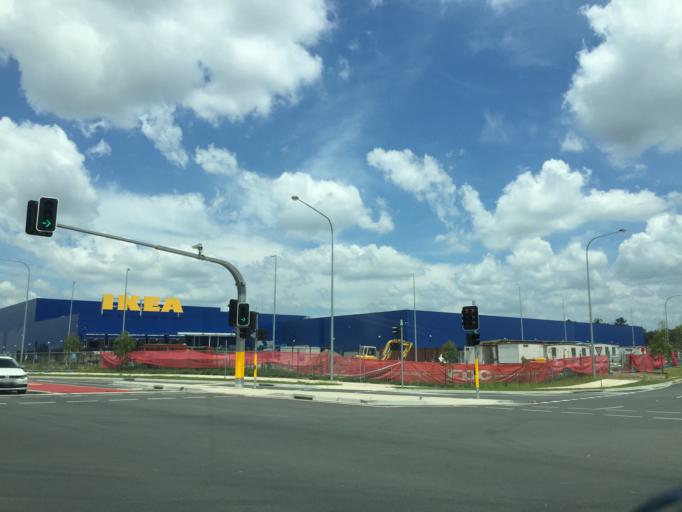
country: AU
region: New South Wales
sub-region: Blacktown
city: Hassall Grove
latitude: -33.7177
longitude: 150.8441
